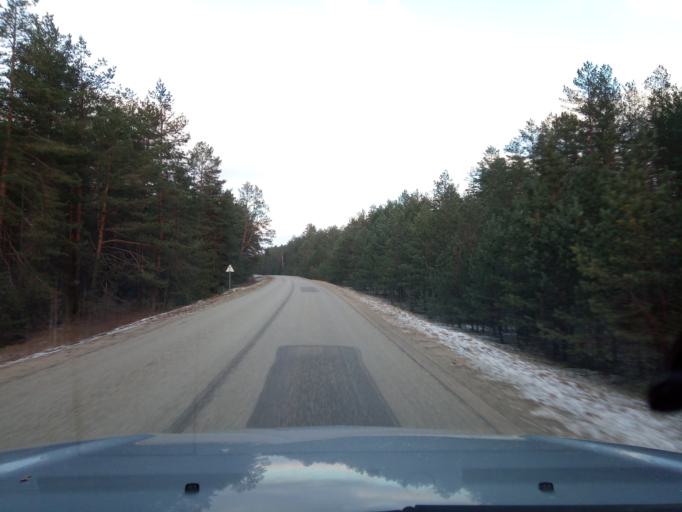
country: LT
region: Alytaus apskritis
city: Varena
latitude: 54.1332
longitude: 24.4665
